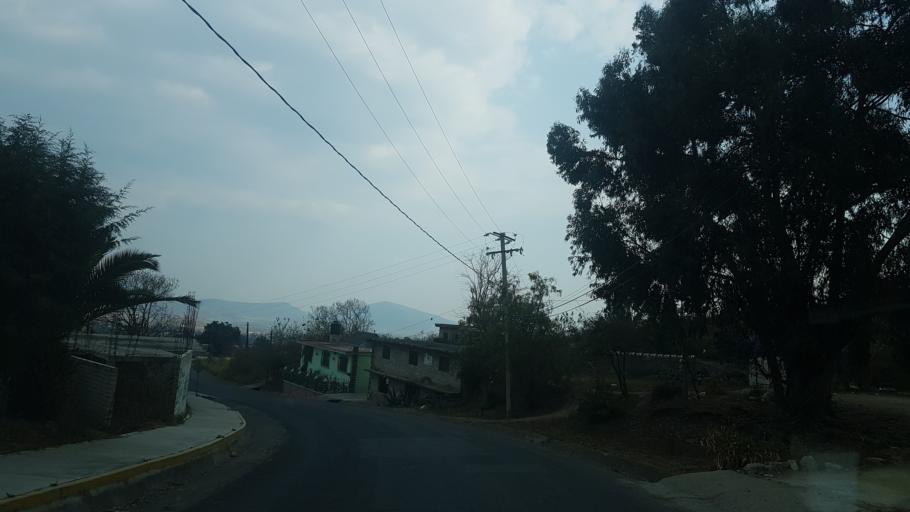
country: MX
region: Puebla
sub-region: Santa Isabel Cholula
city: San Martin Tlamapa
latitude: 18.9765
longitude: -98.3957
